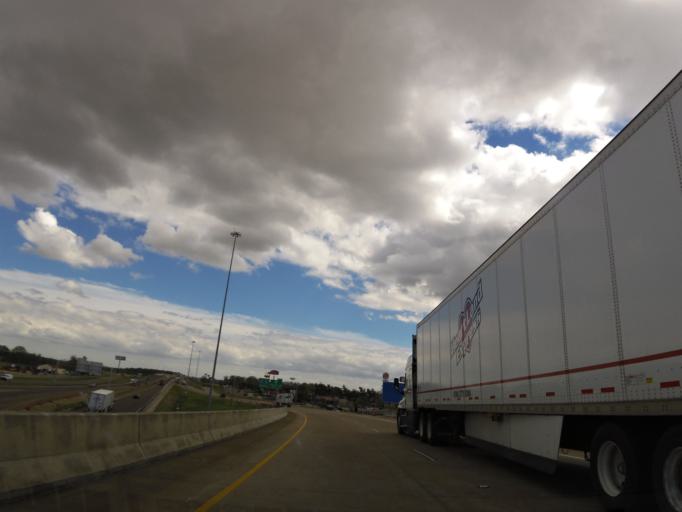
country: US
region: Arkansas
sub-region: Crittenden County
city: West Memphis
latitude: 35.1709
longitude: -90.1923
